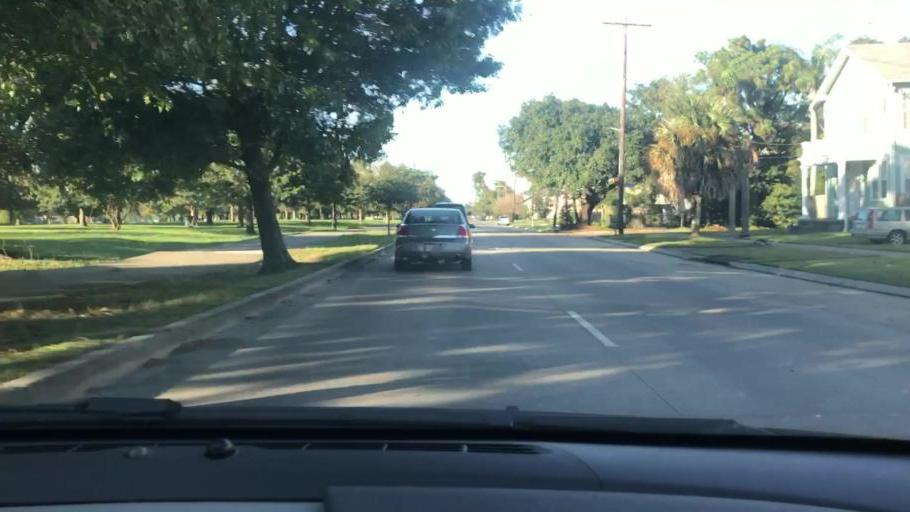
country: US
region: Louisiana
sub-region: Jefferson Parish
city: Metairie
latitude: 30.0060
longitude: -90.1146
